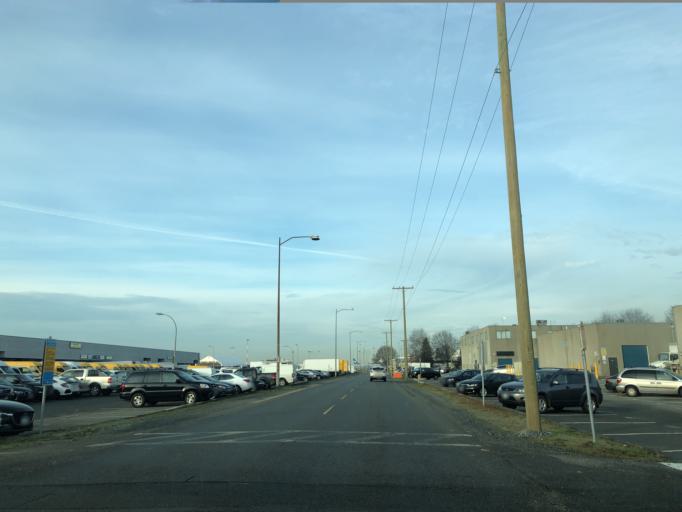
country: CA
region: British Columbia
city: Richmond
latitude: 49.1908
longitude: -123.1715
